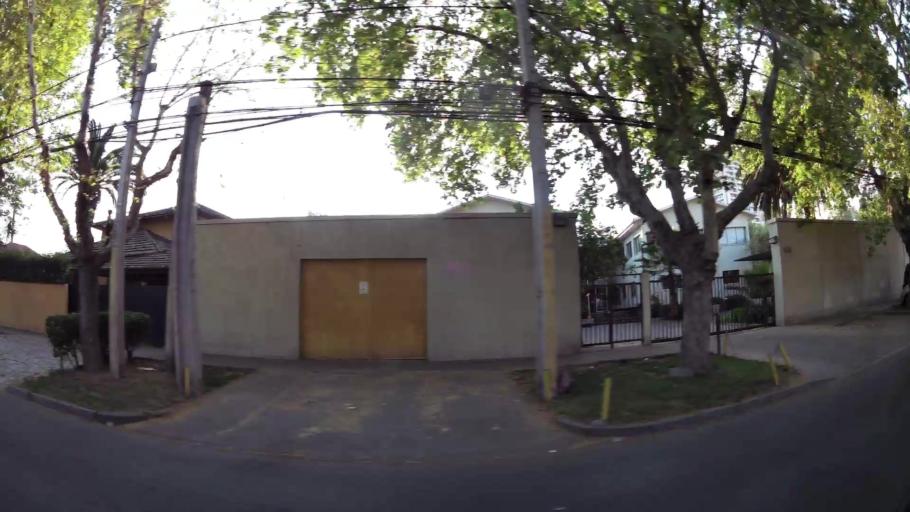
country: CL
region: Santiago Metropolitan
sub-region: Provincia de Santiago
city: Villa Presidente Frei, Nunoa, Santiago, Chile
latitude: -33.4527
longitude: -70.5763
